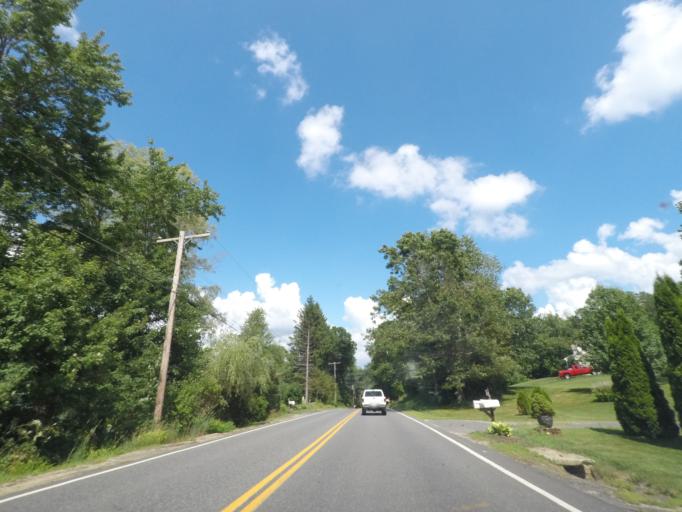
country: US
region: Massachusetts
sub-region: Hampden County
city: Monson Center
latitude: 42.1148
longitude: -72.2771
